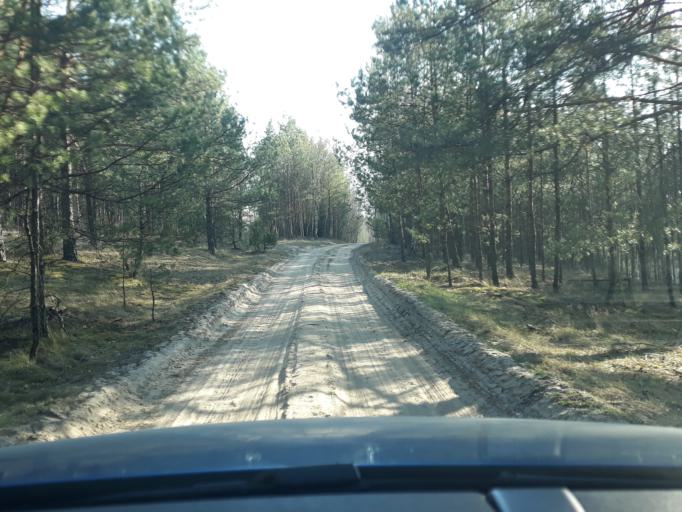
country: PL
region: Pomeranian Voivodeship
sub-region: Powiat bytowski
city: Lipnica
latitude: 53.8888
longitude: 17.4913
